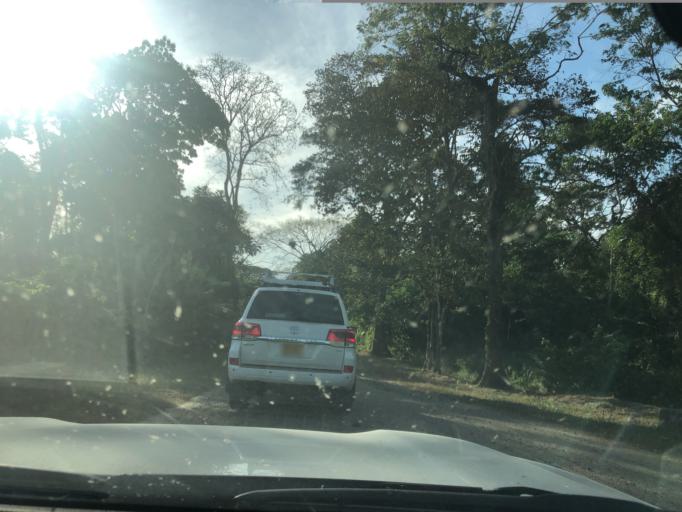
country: NI
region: Rivas
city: Cardenas
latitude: 11.1265
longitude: -85.2989
